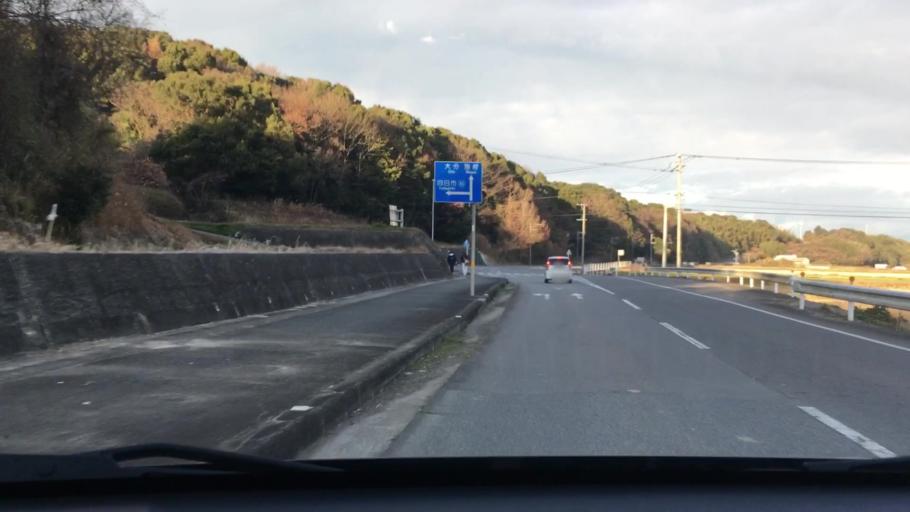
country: JP
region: Oita
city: Bungo-Takada-shi
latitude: 33.5167
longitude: 131.3494
